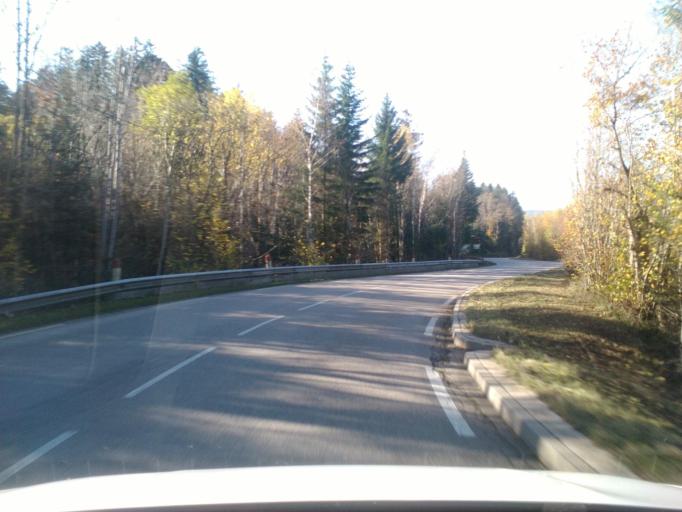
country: FR
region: Lorraine
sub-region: Departement des Vosges
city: Senones
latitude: 48.4080
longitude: 7.0680
